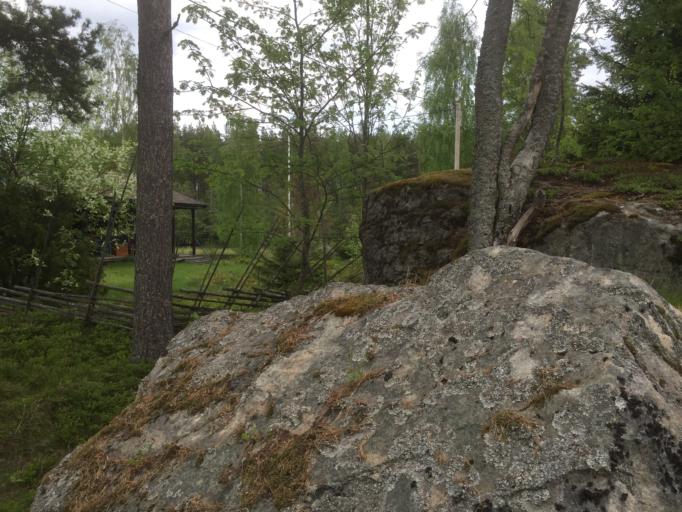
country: SE
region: Uppsala
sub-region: Alvkarleby Kommun
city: Skutskaer
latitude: 60.7905
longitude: 17.2967
